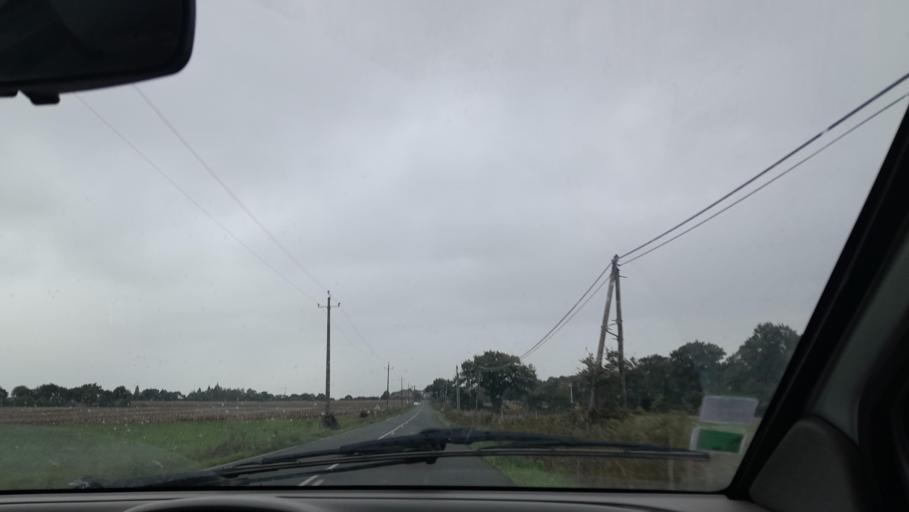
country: FR
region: Pays de la Loire
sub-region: Departement de Maine-et-Loire
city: Pouance
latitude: 47.7259
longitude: -1.1777
